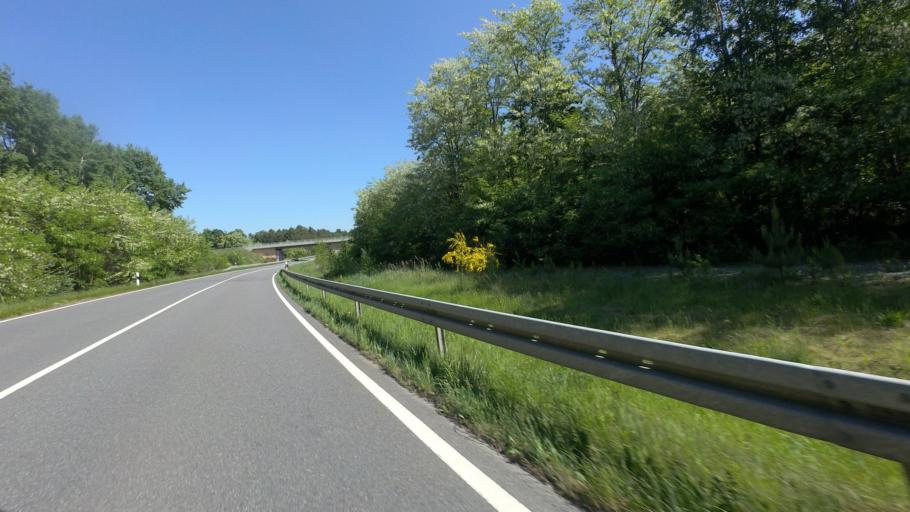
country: DE
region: Brandenburg
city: Spremberg
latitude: 51.5806
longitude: 14.3408
